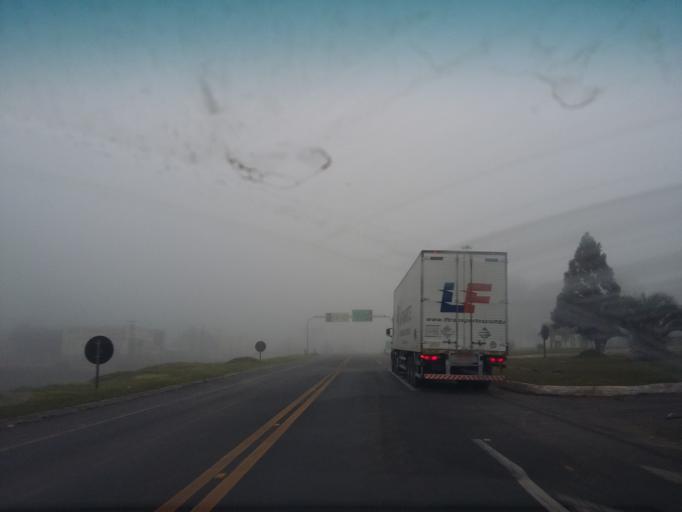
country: BR
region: Santa Catarina
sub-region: Curitibanos
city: Curitibanos
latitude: -27.3031
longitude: -50.4228
